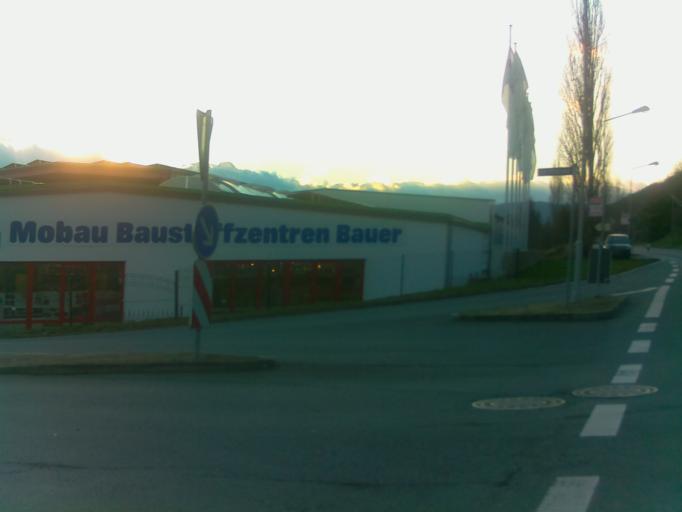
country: DE
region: Thuringia
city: Rudolstadt
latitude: 50.7285
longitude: 11.3714
